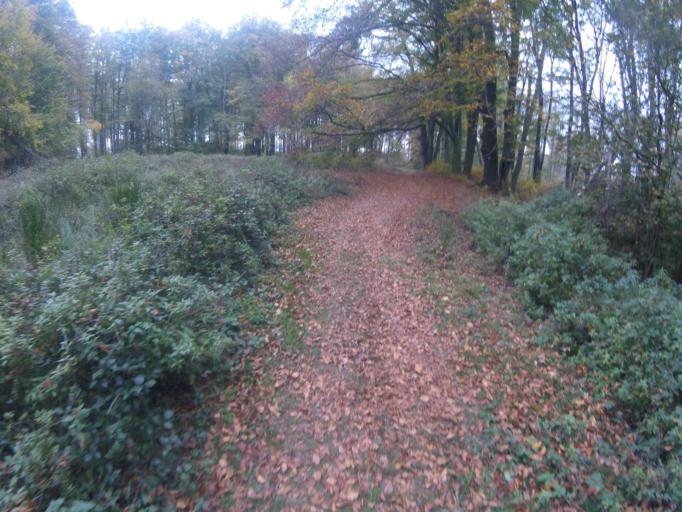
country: HU
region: Veszprem
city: Zirc
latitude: 47.2655
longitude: 17.7455
